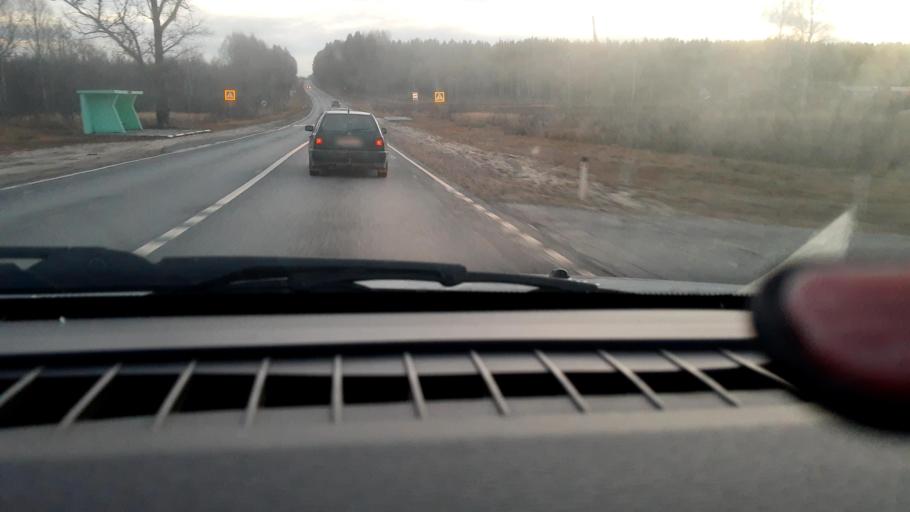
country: RU
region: Nizjnij Novgorod
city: Krasnyye Baki
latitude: 57.0443
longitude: 45.1319
